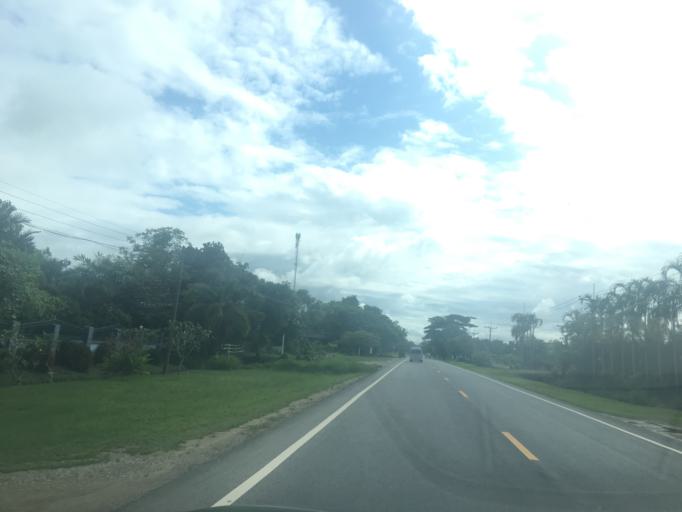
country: TH
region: Chiang Rai
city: Mae Lao
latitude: 19.8397
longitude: 99.7176
